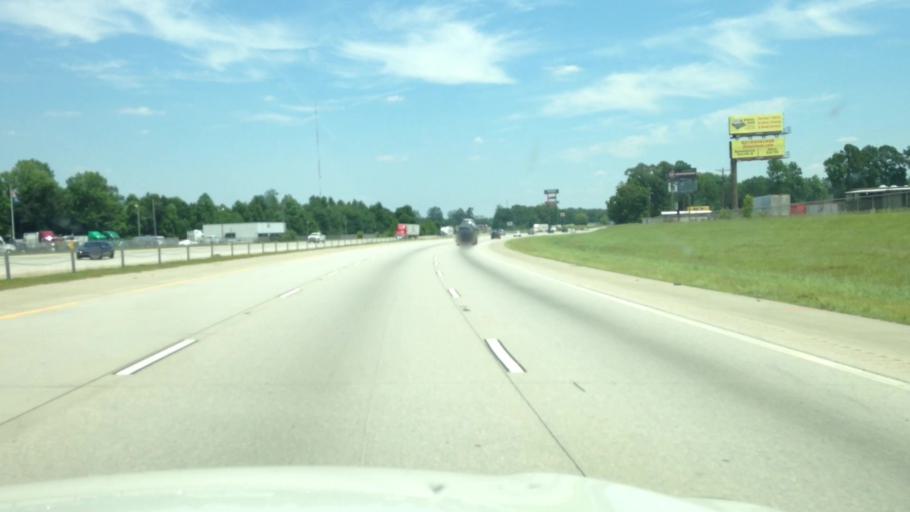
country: US
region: South Carolina
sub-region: Florence County
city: Florence
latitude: 34.2639
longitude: -79.7429
